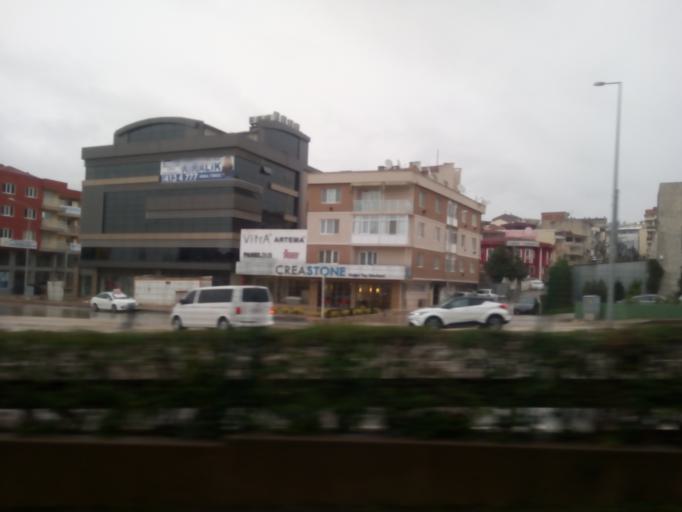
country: TR
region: Bursa
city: Yildirim
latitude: 40.2347
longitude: 28.9788
